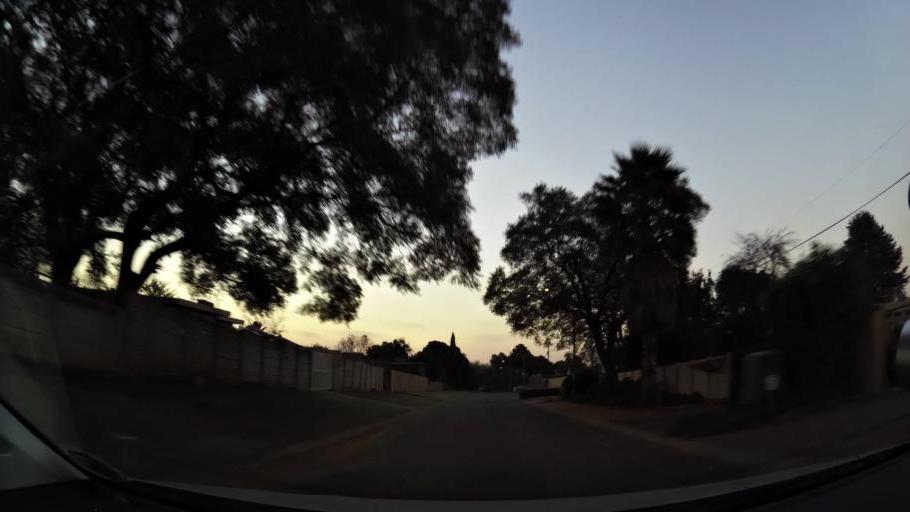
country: ZA
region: Gauteng
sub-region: Ekurhuleni Metropolitan Municipality
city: Tembisa
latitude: -26.0498
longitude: 28.2445
